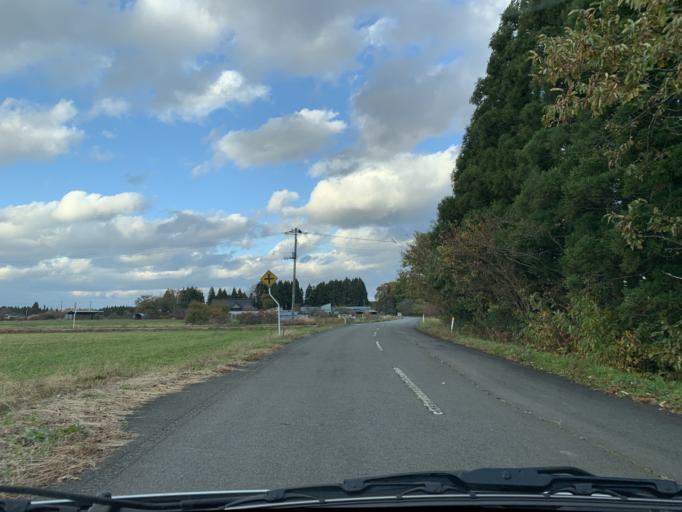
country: JP
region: Iwate
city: Mizusawa
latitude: 39.0973
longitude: 141.0136
